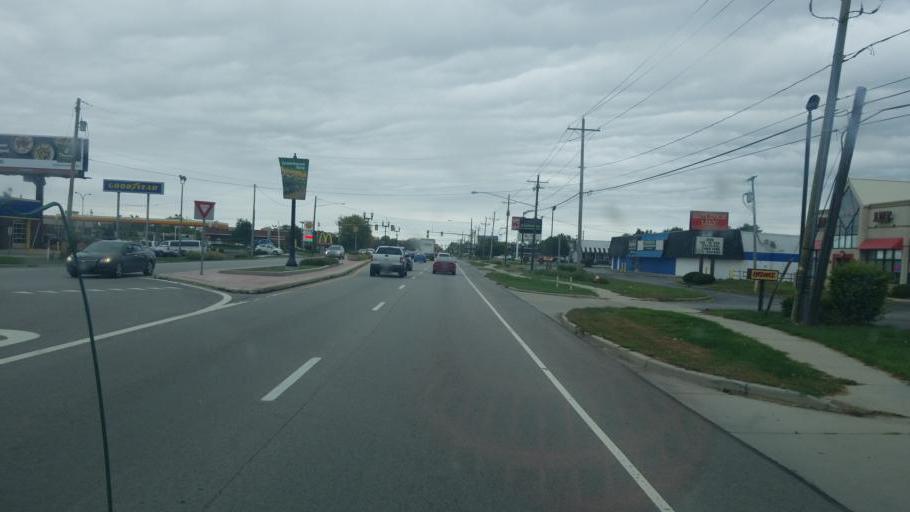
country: US
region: Ohio
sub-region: Lucas County
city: Maumee
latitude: 41.5989
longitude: -83.6646
